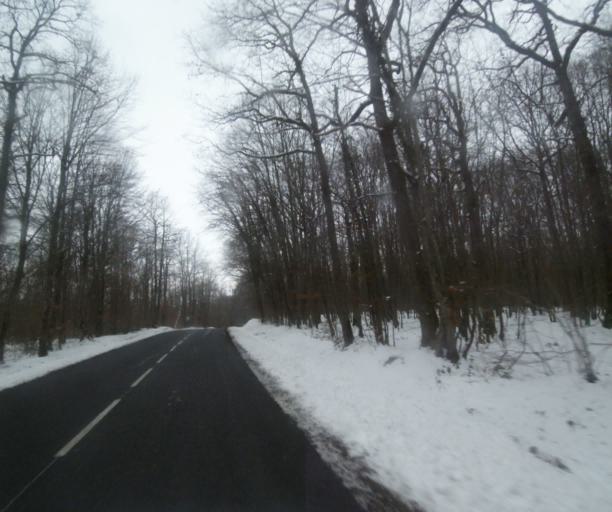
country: FR
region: Champagne-Ardenne
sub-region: Departement de la Haute-Marne
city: Laneuville-a-Remy
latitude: 48.4443
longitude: 4.8607
